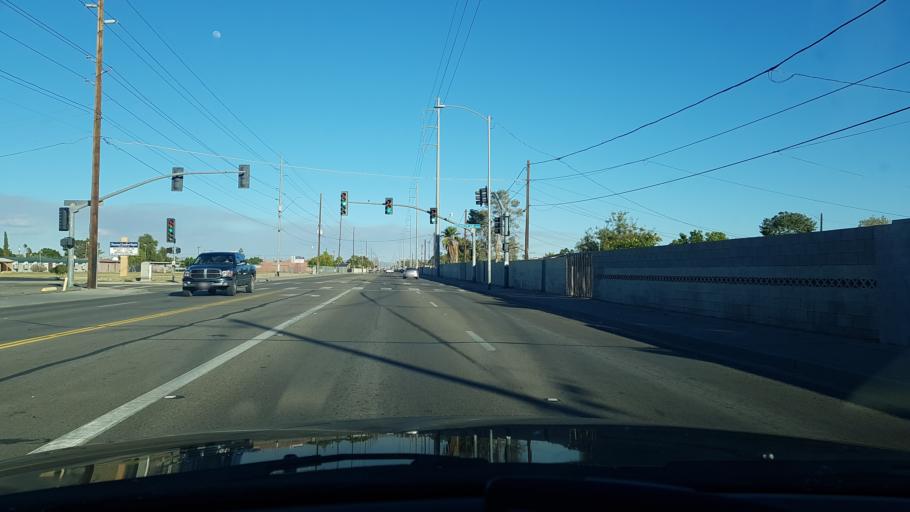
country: US
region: Arizona
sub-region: Yuma County
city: Yuma
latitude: 32.6839
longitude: -114.6103
